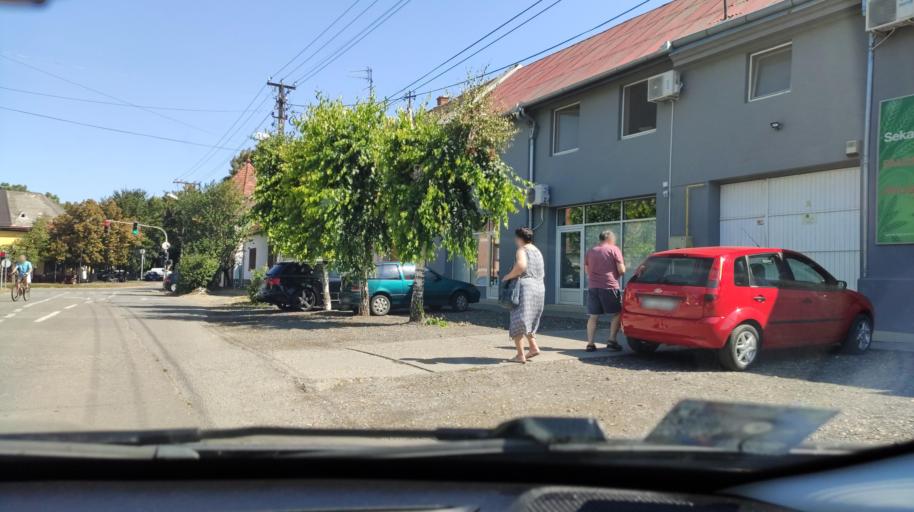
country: RS
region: Autonomna Pokrajina Vojvodina
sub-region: Severnobacki Okrug
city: Backa Topola
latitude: 45.8130
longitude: 19.6362
